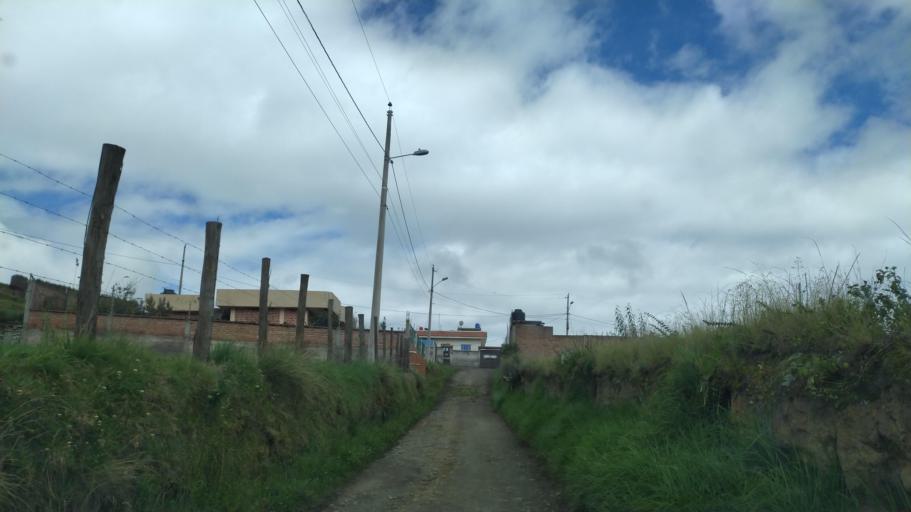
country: EC
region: Chimborazo
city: Riobamba
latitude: -1.6656
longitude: -78.5733
